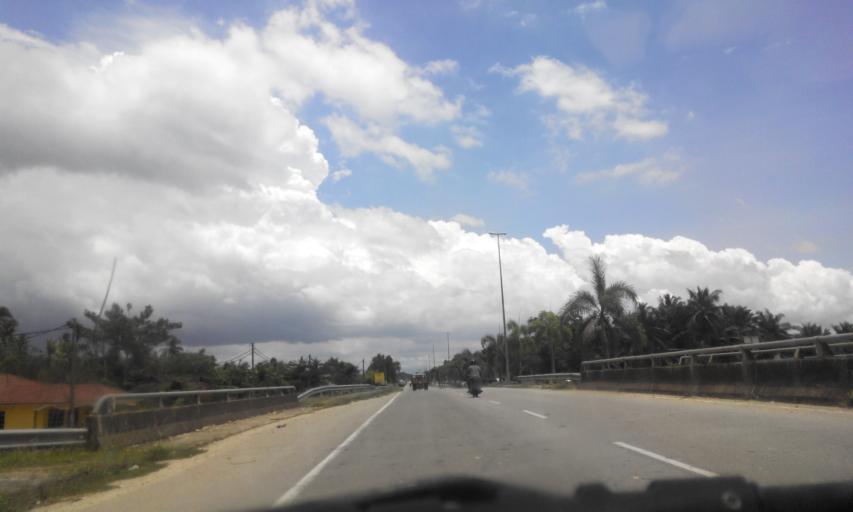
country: MY
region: Perak
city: Parit Buntar
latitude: 5.1191
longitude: 100.5223
